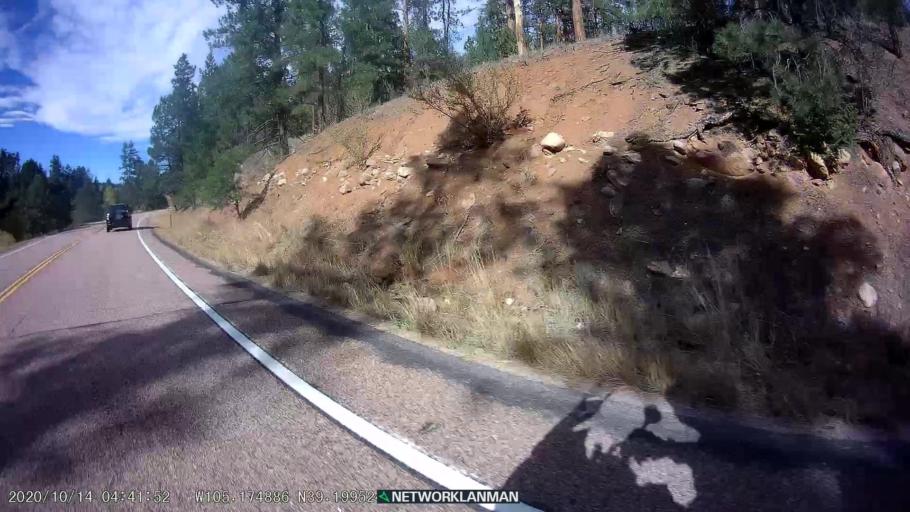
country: US
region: Colorado
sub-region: Douglas County
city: Perry Park
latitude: 39.1997
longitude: -105.1750
